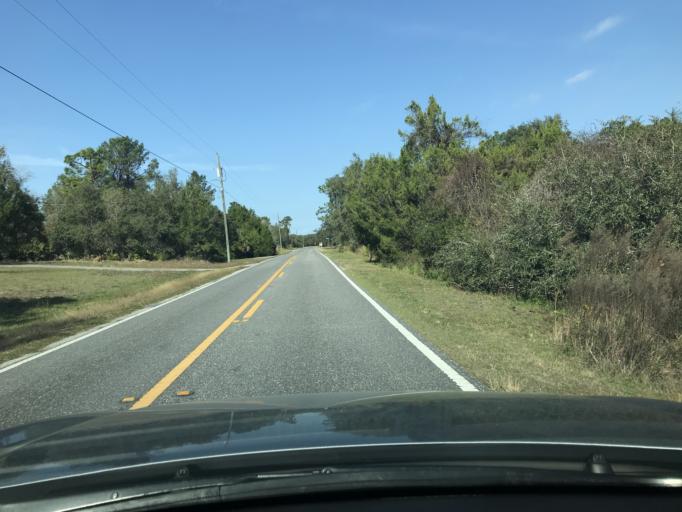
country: US
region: Florida
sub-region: Hernando County
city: North Weeki Wachee
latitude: 28.5495
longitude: -82.5527
